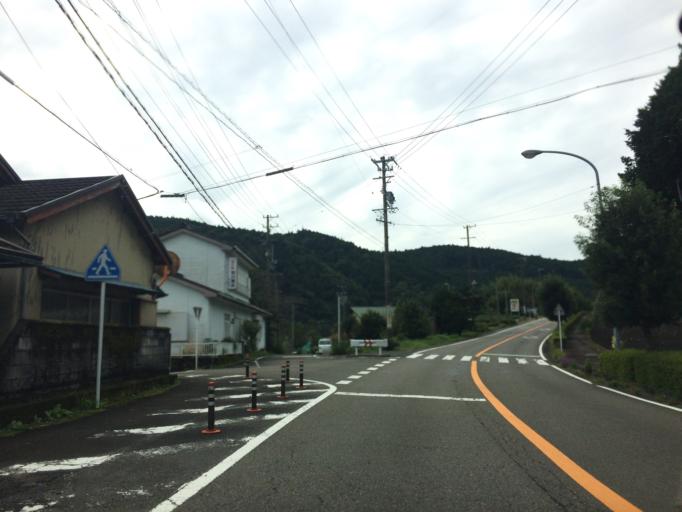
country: JP
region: Shizuoka
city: Fujieda
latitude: 35.0927
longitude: 138.1275
